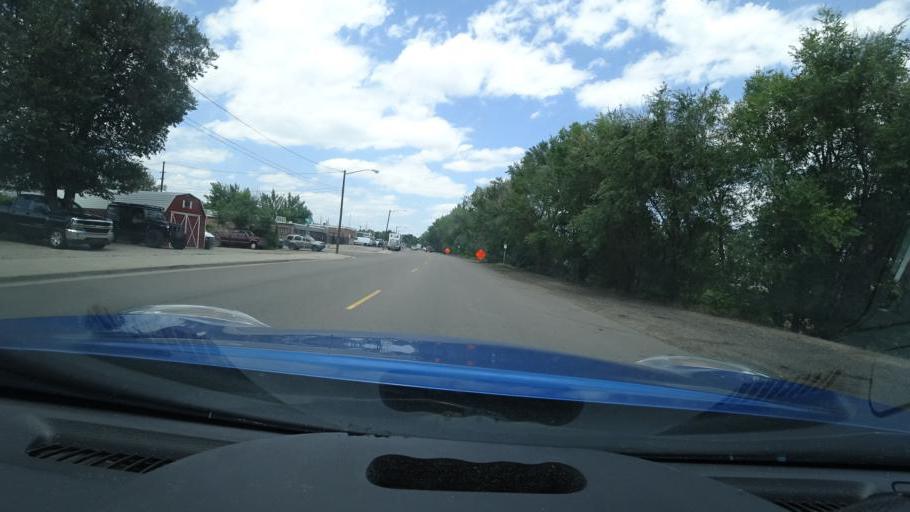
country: US
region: Colorado
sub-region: Arapahoe County
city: Englewood
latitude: 39.6761
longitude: -104.9981
